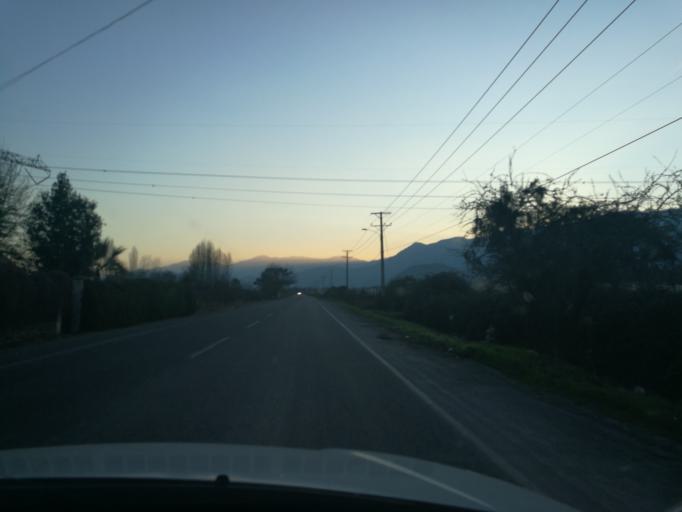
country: CL
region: O'Higgins
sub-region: Provincia de Cachapoal
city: Graneros
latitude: -34.0350
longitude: -70.6762
